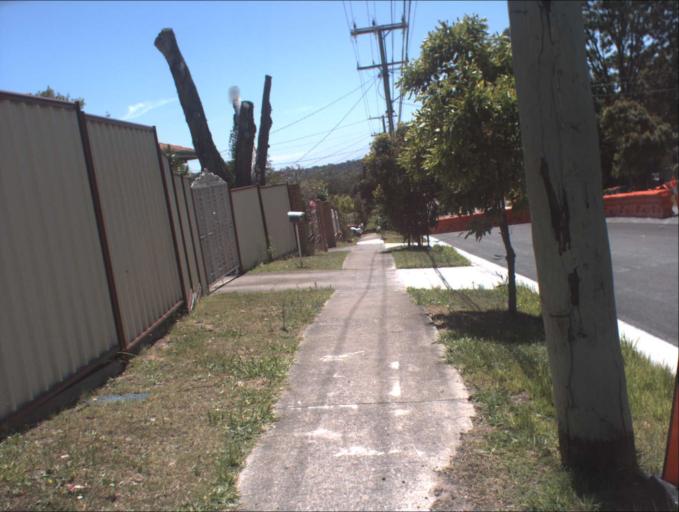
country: AU
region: Queensland
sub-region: Logan
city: Woodridge
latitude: -27.6270
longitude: 153.1098
